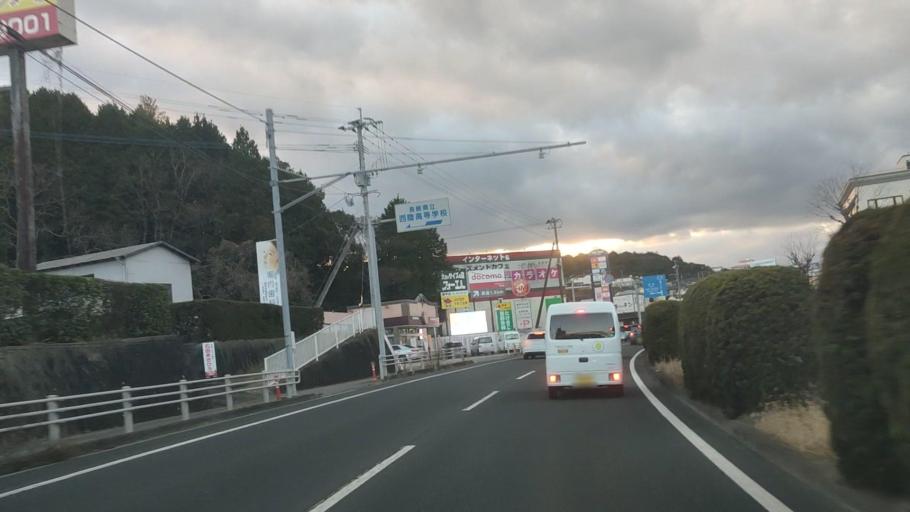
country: JP
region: Nagasaki
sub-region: Isahaya-shi
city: Isahaya
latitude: 32.8295
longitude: 129.9988
